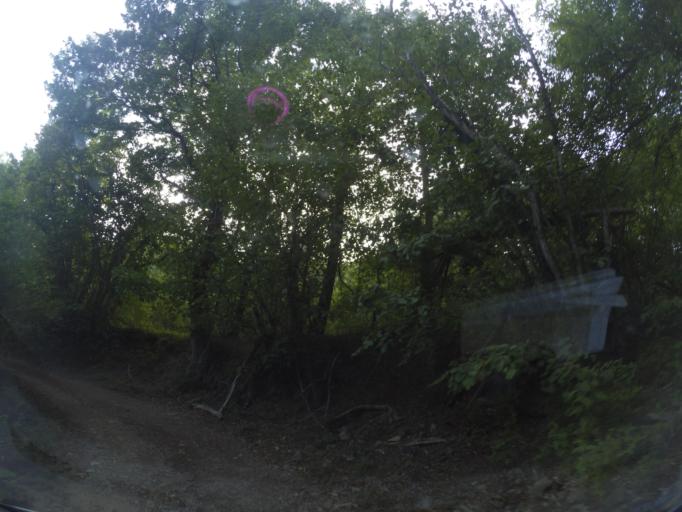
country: IT
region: Tuscany
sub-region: Province of Arezzo
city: Castiglion Fibocchi
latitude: 43.5591
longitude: 11.7819
